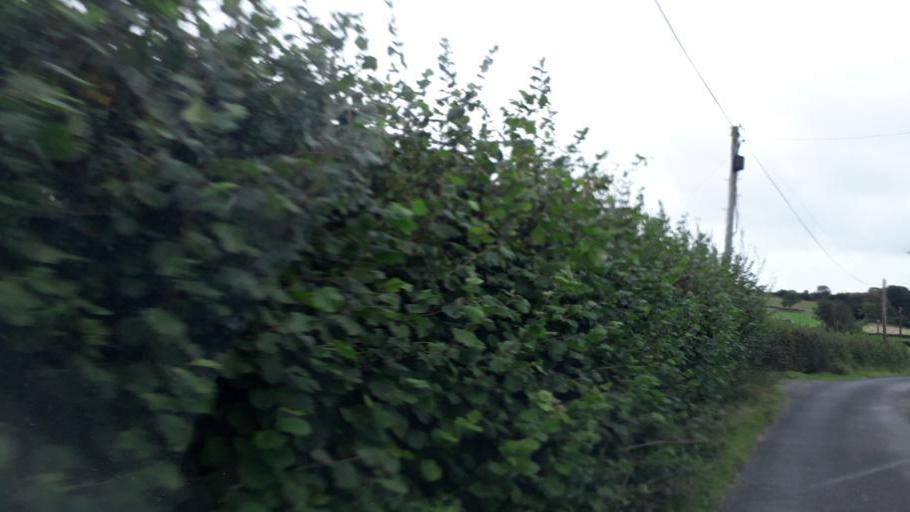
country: IE
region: Leinster
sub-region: Wicklow
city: Enniskerry
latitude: 53.1661
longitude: -6.1959
